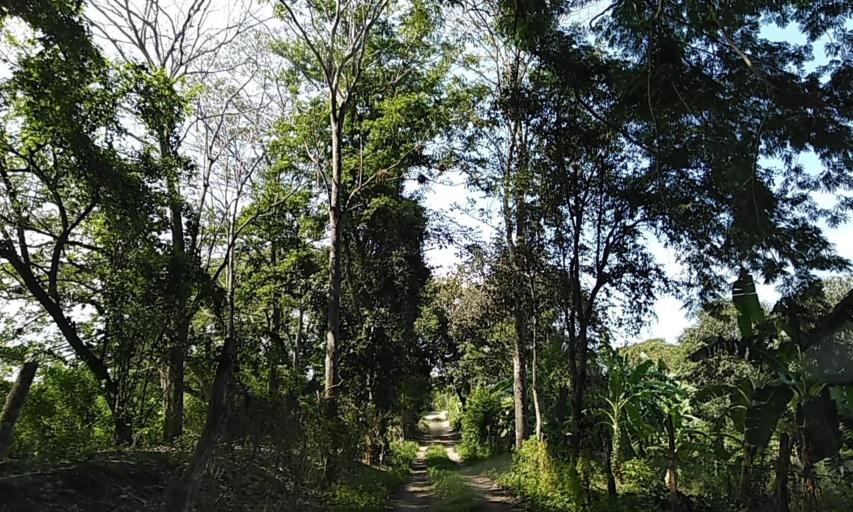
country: MX
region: Veracruz
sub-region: Emiliano Zapata
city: Plan del Rio
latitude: 19.4494
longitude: -96.6775
